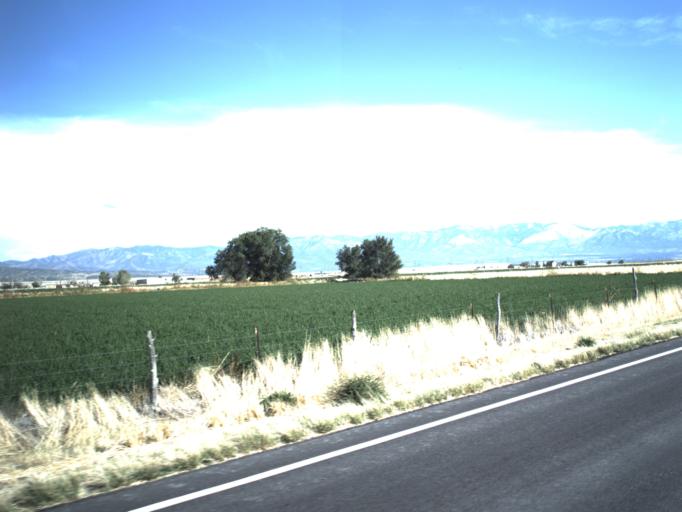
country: US
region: Utah
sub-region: Millard County
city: Delta
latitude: 39.2075
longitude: -112.4124
